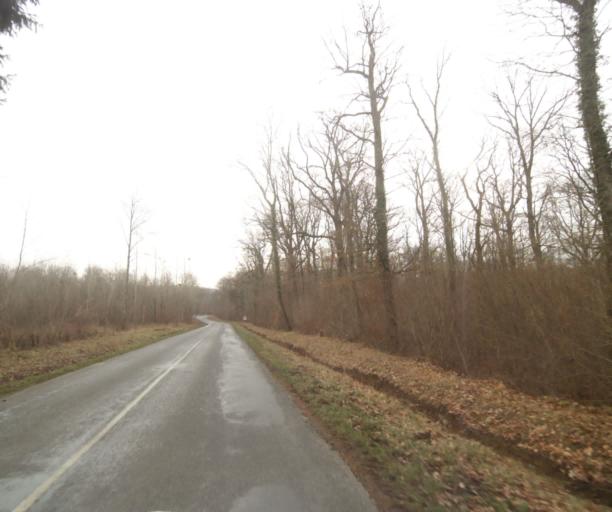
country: FR
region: Champagne-Ardenne
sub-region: Departement de la Marne
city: Pargny-sur-Saulx
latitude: 48.7338
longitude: 4.8625
